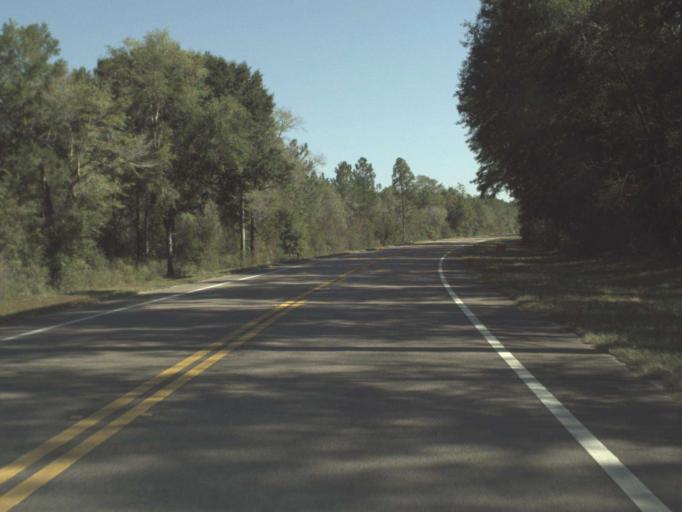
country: US
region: Florida
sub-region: Walton County
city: Freeport
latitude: 30.4783
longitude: -85.9609
